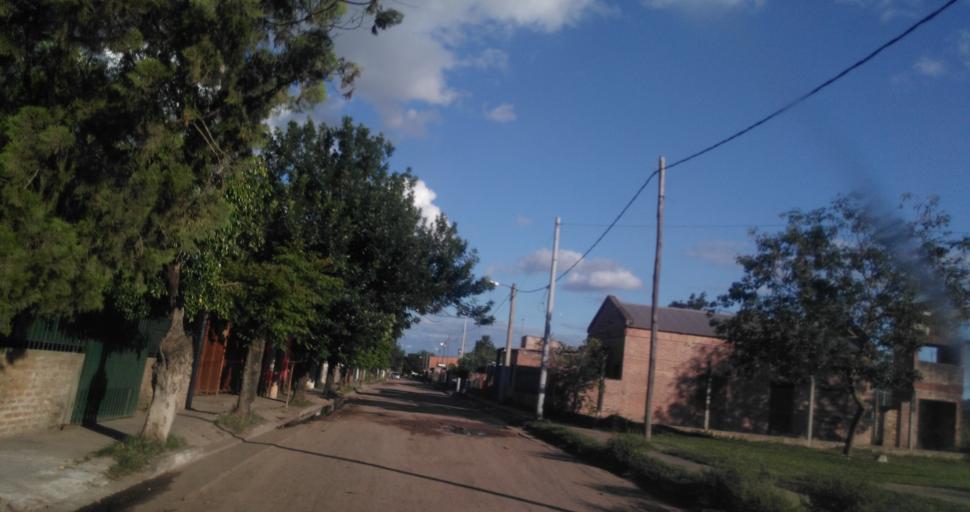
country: AR
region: Chaco
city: Fontana
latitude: -27.4226
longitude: -59.0324
